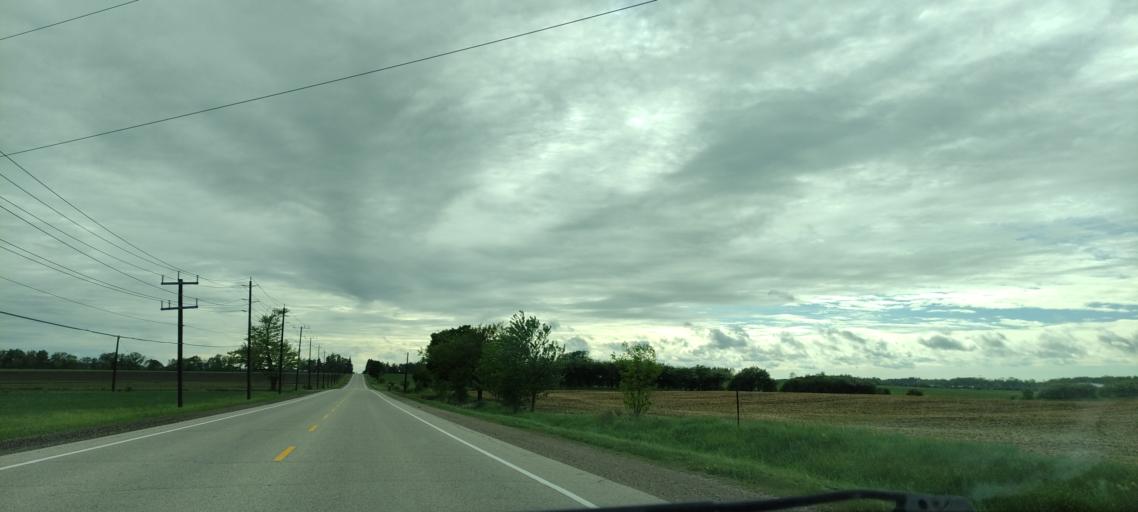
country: CA
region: Ontario
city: Kitchener
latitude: 43.3802
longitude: -80.6640
